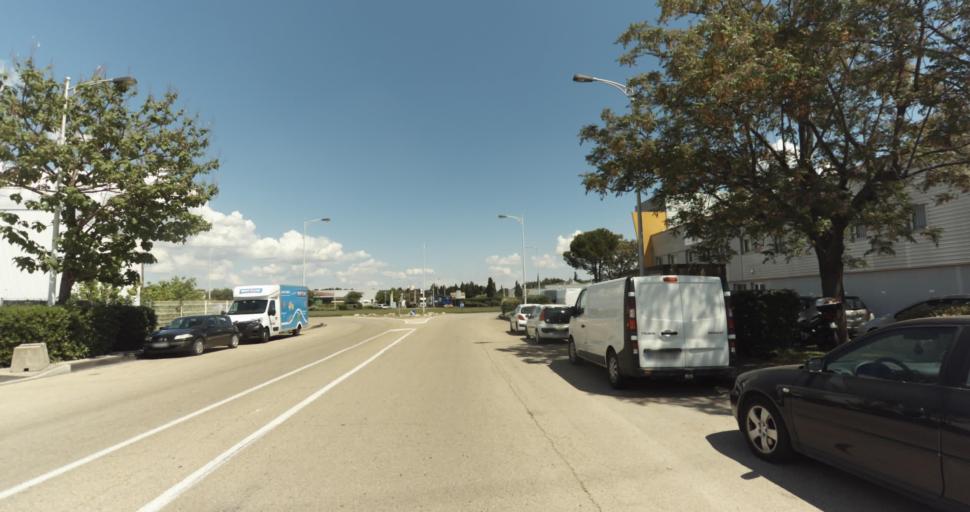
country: FR
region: Languedoc-Roussillon
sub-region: Departement du Gard
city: Nimes
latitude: 43.8112
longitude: 4.3383
